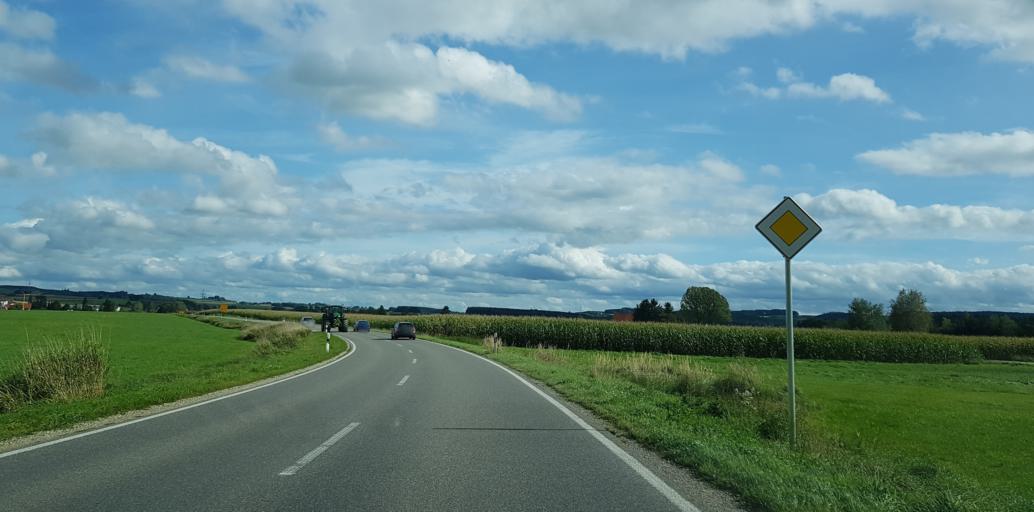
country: DE
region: Baden-Wuerttemberg
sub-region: Tuebingen Region
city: Eberhardzell
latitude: 47.9664
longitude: 9.8024
